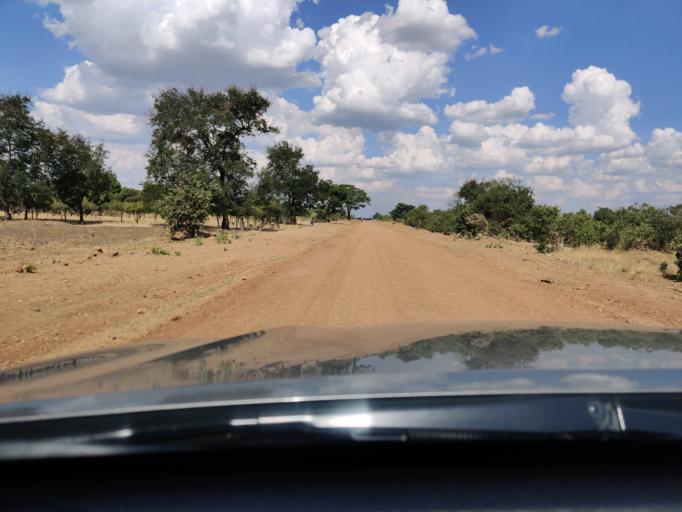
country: ZM
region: Central
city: Chibombo
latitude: -14.7592
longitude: 27.8702
